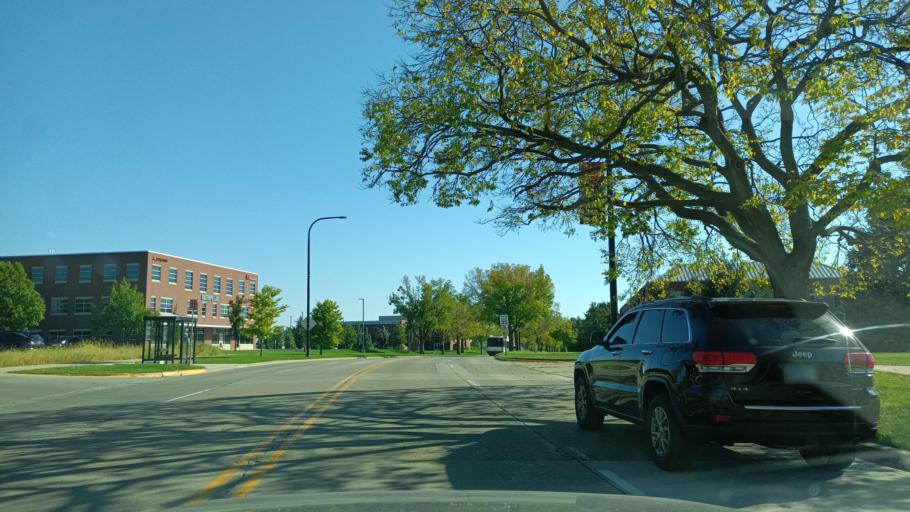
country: US
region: Illinois
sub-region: Champaign County
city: Champaign
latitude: 40.0934
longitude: -88.2385
